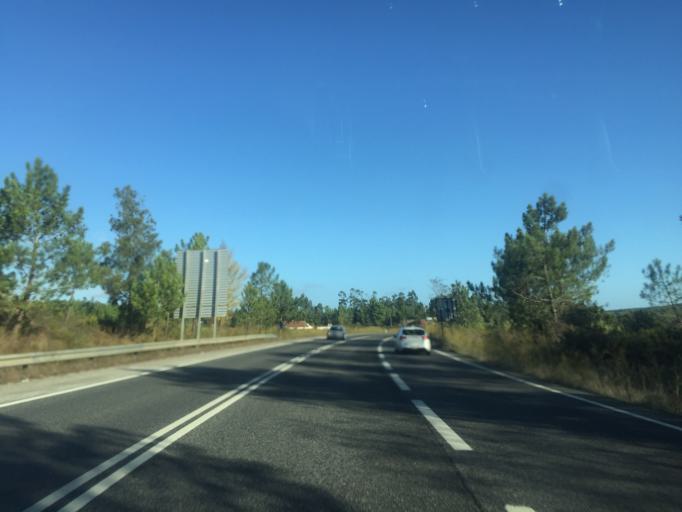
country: PT
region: Lisbon
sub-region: Azambuja
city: Alcoentre
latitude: 39.2396
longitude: -8.9564
